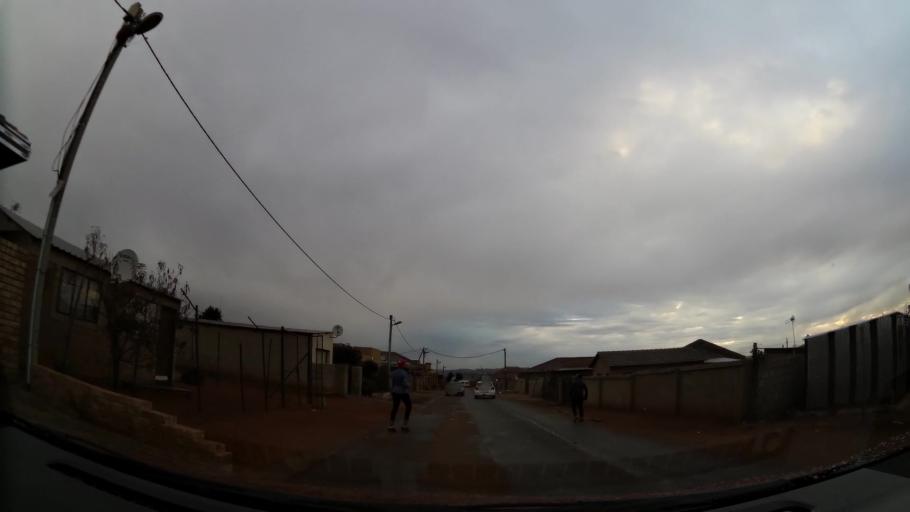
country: ZA
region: Gauteng
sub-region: City of Johannesburg Metropolitan Municipality
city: Roodepoort
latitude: -26.1725
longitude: 27.7882
